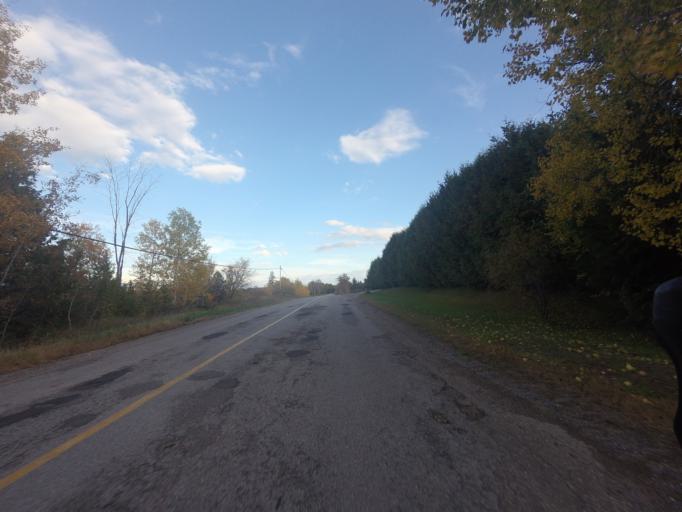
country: CA
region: Ontario
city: Pembroke
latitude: 45.5241
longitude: -77.0796
